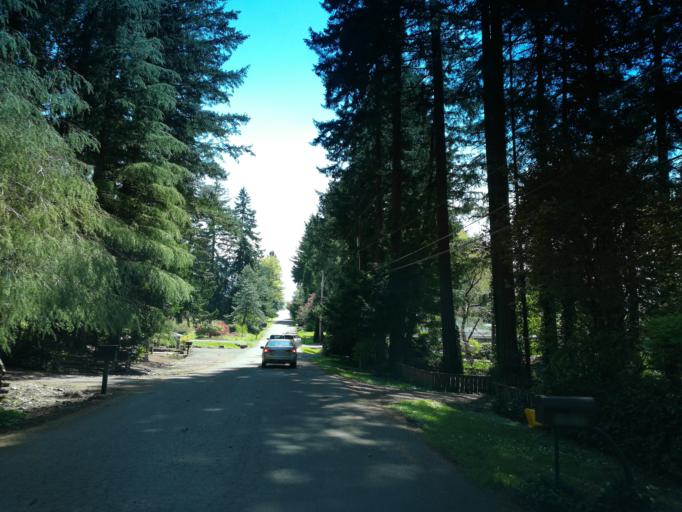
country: US
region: Oregon
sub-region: Clackamas County
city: Damascus
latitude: 45.4361
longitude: -122.4178
